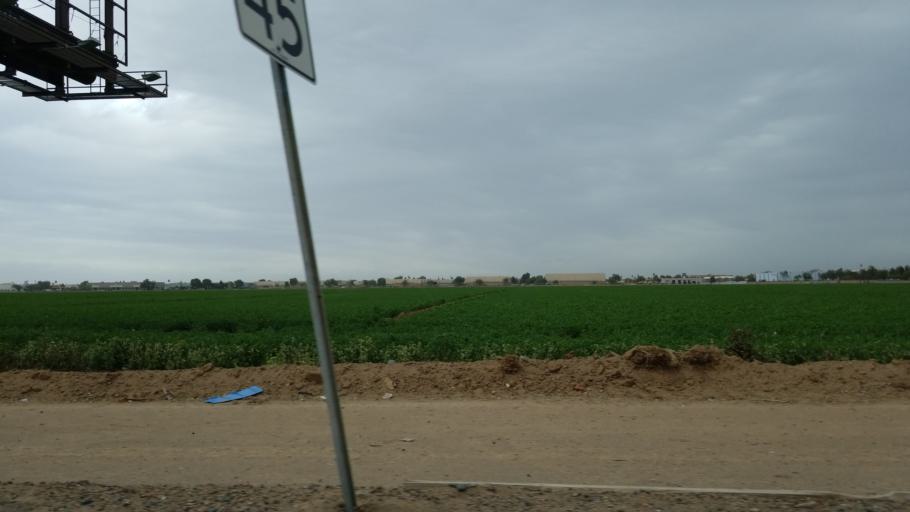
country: US
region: Arizona
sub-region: Maricopa County
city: Tolleson
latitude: 33.4514
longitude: -112.1752
